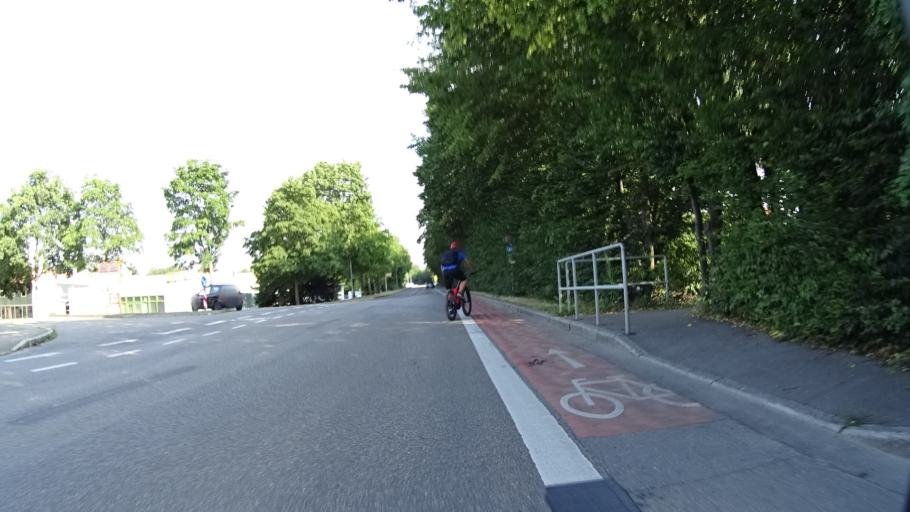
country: DE
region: Baden-Wuerttemberg
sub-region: Regierungsbezirk Stuttgart
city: Eislingen
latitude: 48.6943
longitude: 9.6787
